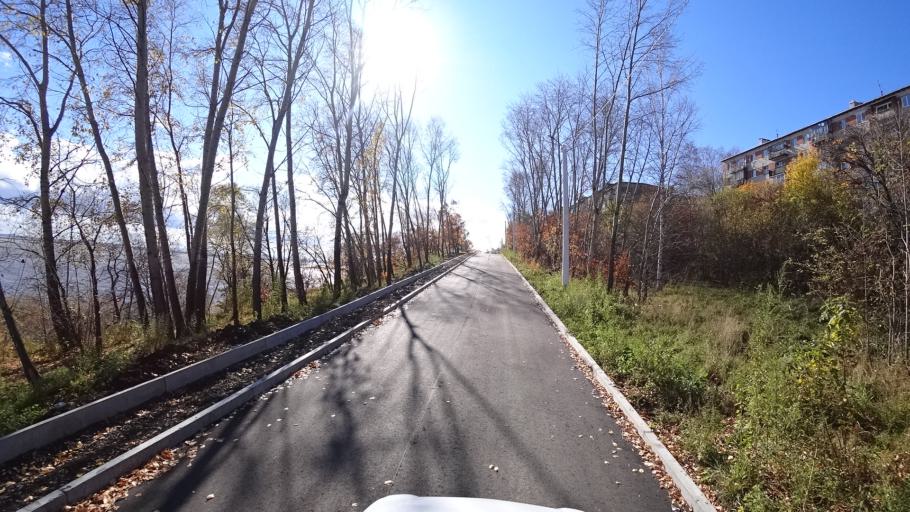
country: RU
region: Khabarovsk Krai
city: Amursk
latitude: 50.2164
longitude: 136.9069
